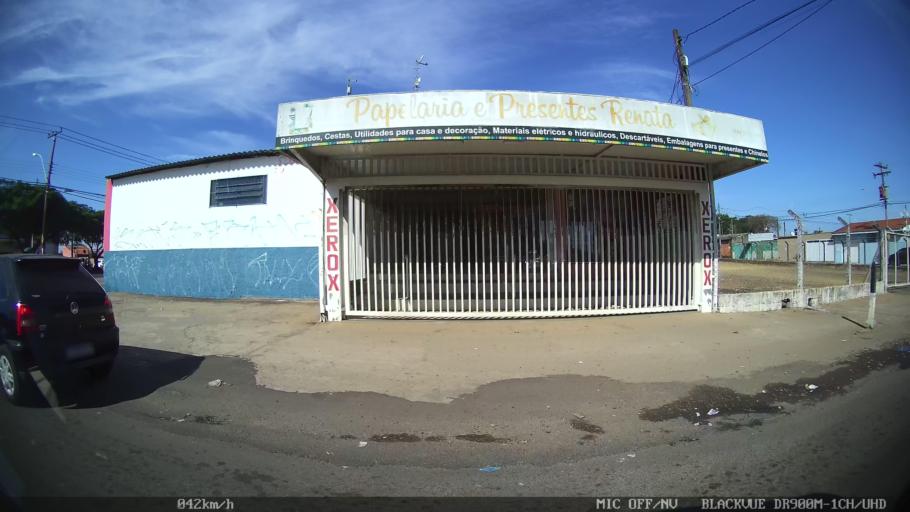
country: BR
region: Sao Paulo
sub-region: Franca
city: Franca
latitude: -20.5008
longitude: -47.4138
